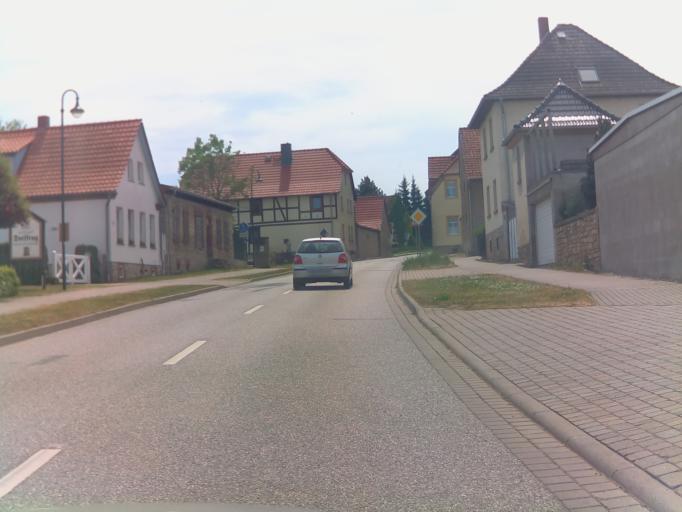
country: DE
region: Saxony-Anhalt
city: Hedersleben
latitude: 51.8395
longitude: 11.2443
